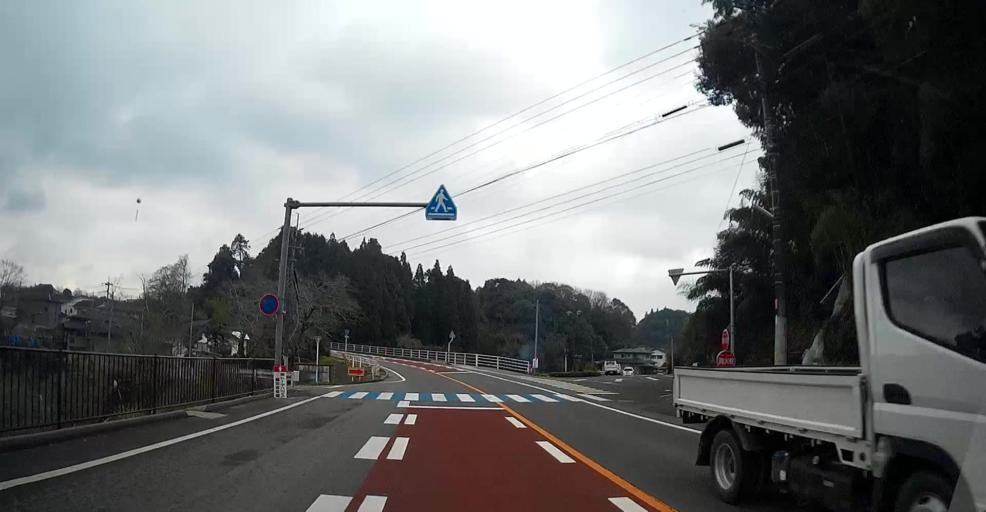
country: JP
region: Kumamoto
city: Matsubase
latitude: 32.6434
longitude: 130.7367
